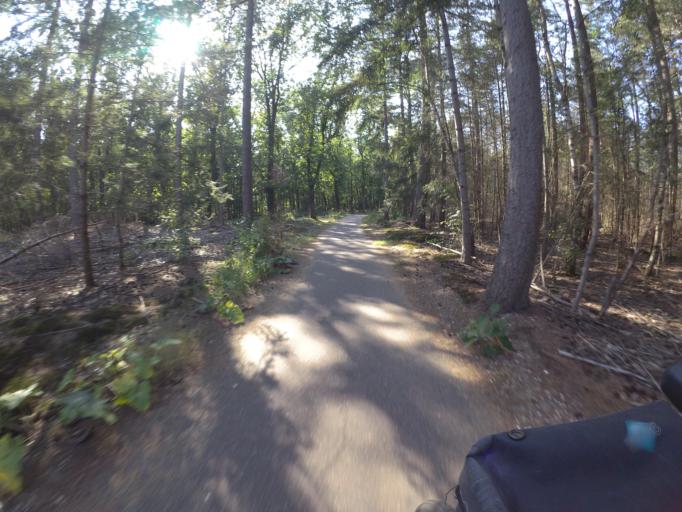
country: NL
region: North Brabant
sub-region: Gemeente Uden
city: Uden
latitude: 51.6826
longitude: 5.6449
